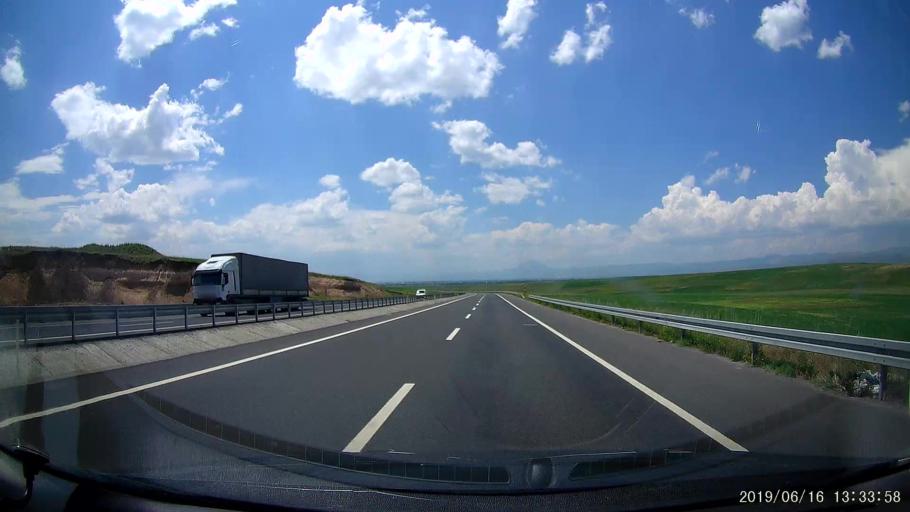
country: TR
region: Agri
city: Agri
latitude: 39.7102
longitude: 43.1397
